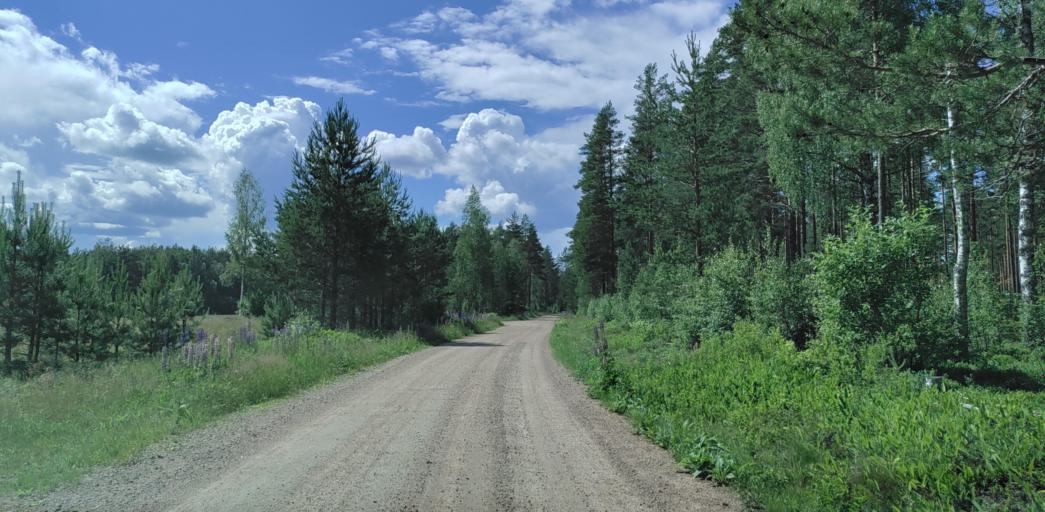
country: SE
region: Vaermland
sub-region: Munkfors Kommun
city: Munkfors
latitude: 59.9610
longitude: 13.5148
